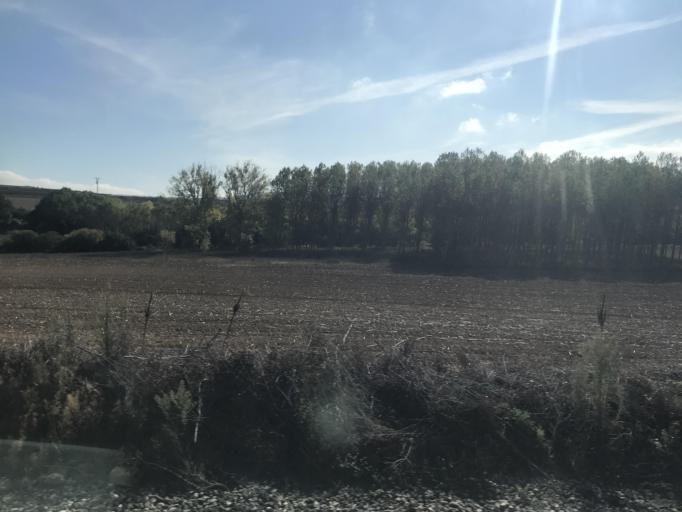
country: ES
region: Basque Country
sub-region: Provincia de Alava
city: Arminon
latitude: 42.7758
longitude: -2.8295
